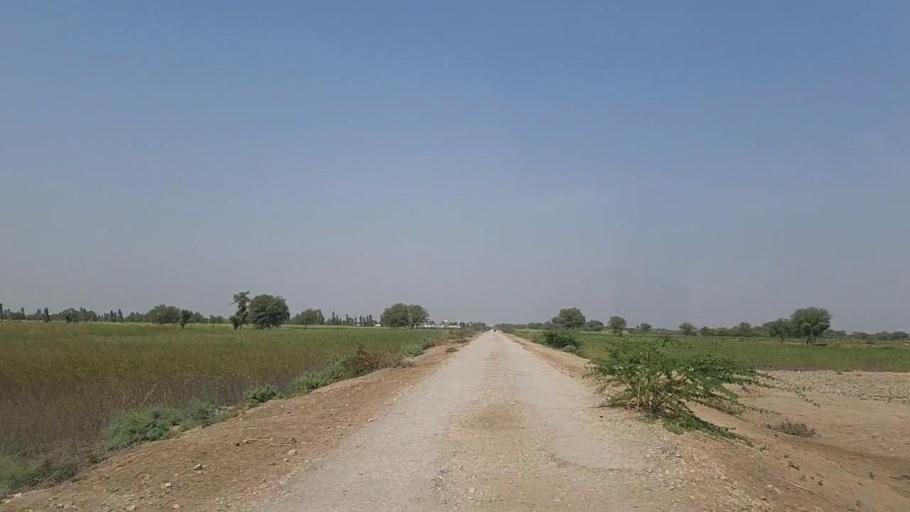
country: PK
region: Sindh
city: Samaro
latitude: 25.2609
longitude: 69.3947
